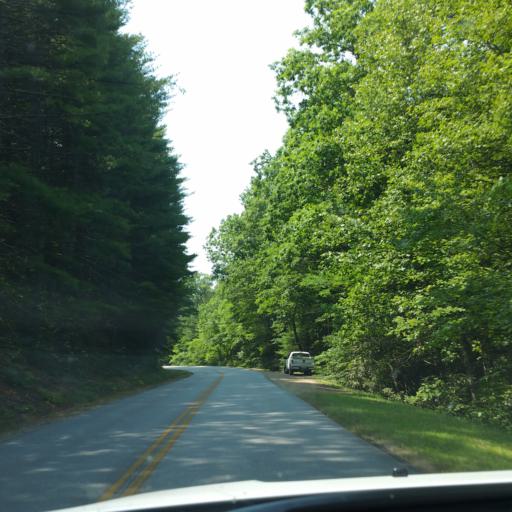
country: US
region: North Carolina
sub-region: Buncombe County
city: Biltmore Forest
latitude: 35.5038
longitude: -82.5583
